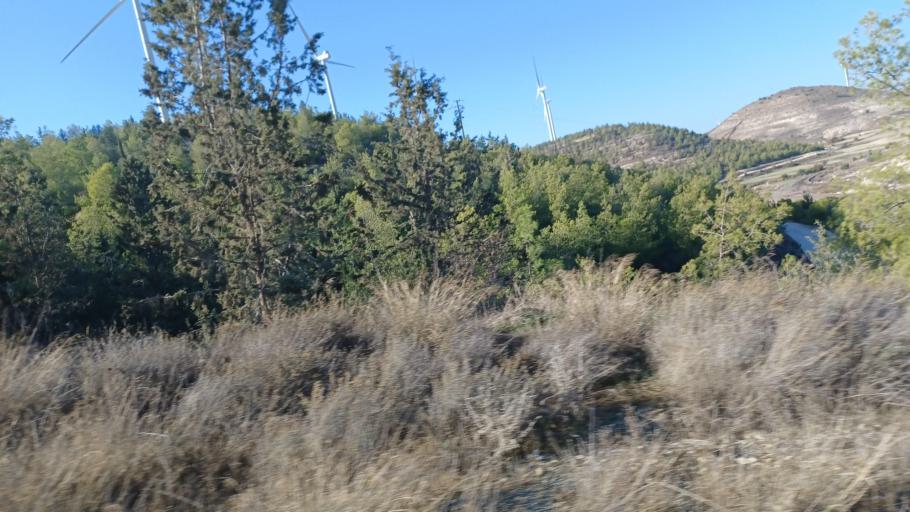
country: CY
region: Larnaka
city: Psevdas
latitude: 34.9602
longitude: 33.5152
